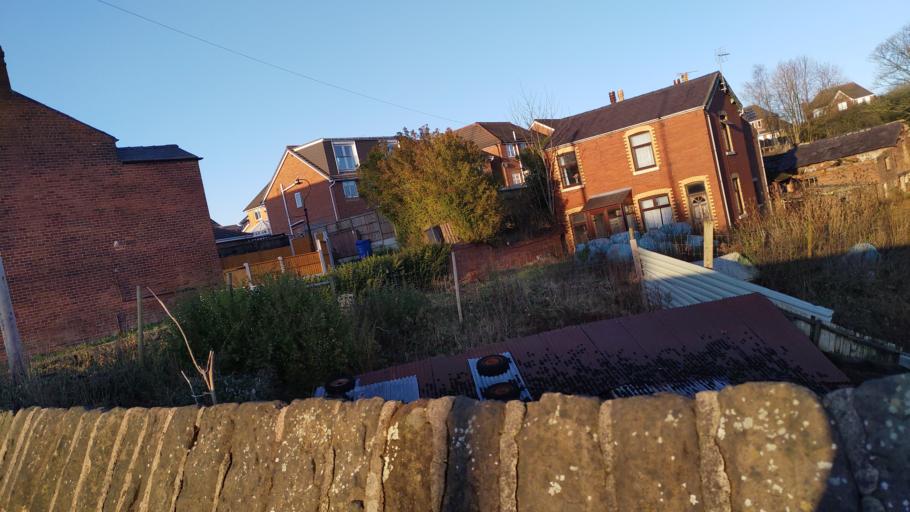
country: GB
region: England
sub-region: Lancashire
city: Adlington
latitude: 53.6217
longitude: -2.6040
